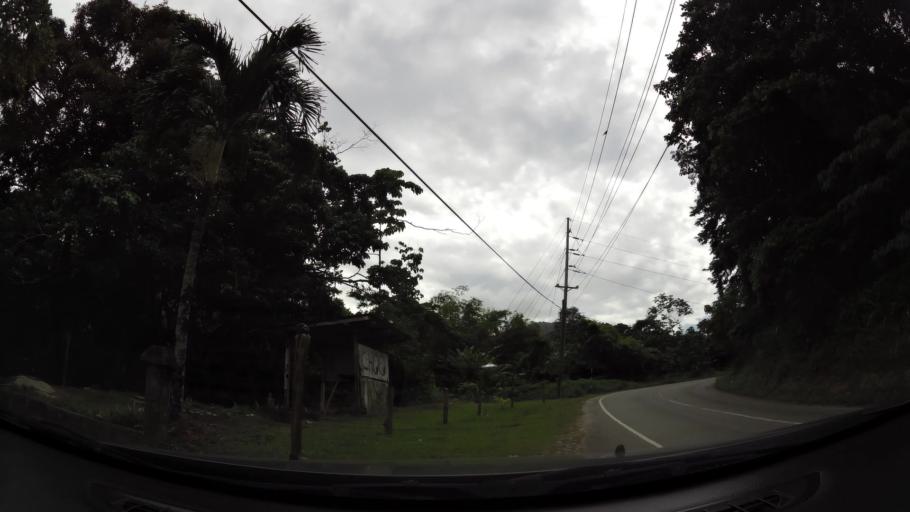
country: TT
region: Diego Martin
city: Petit Valley
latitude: 10.7583
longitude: -61.4442
